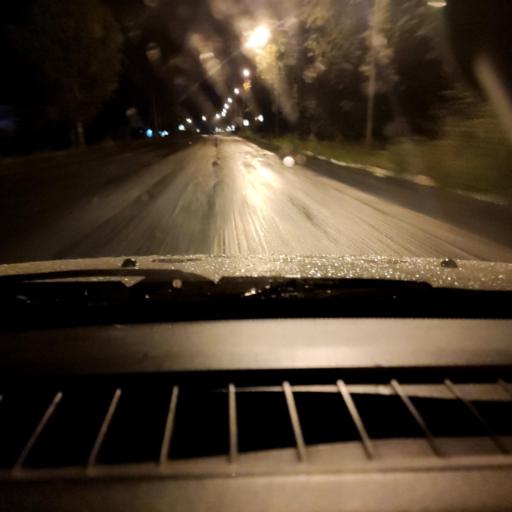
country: RU
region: Udmurtiya
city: Khokhryaki
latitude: 57.1859
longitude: 53.1545
